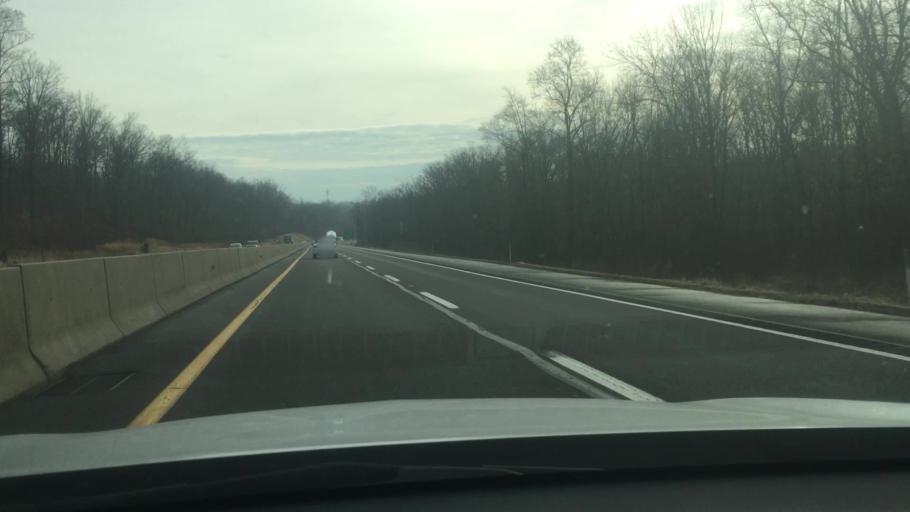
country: US
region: Pennsylvania
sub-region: Lancaster County
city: Mountain Top
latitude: 40.1745
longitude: -75.9198
